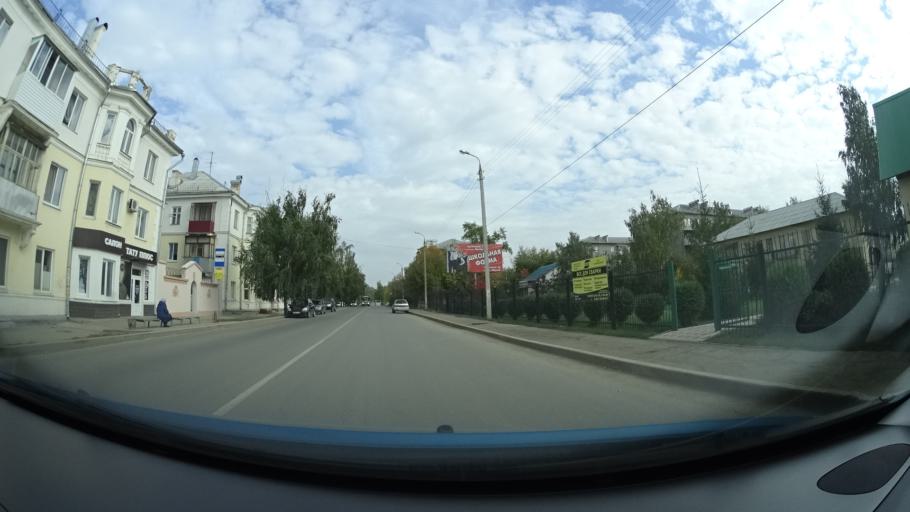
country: RU
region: Bashkortostan
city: Oktyabr'skiy
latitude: 54.4893
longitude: 53.4589
